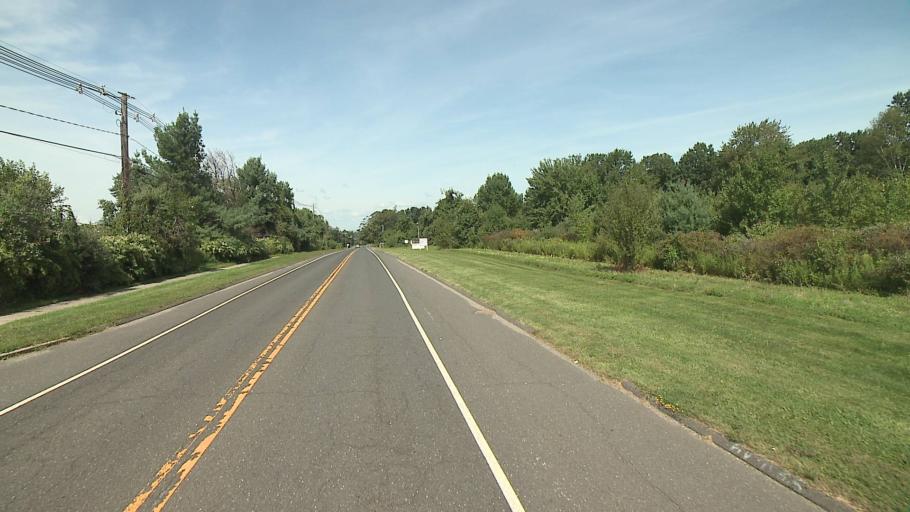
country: US
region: Connecticut
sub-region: Litchfield County
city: Watertown
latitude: 41.6148
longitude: -73.0987
